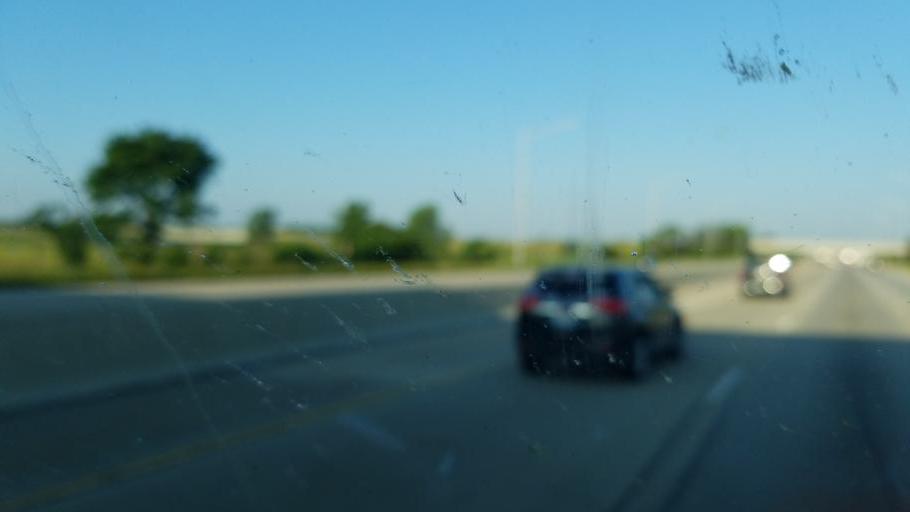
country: US
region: Illinois
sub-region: Will County
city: New Lenox
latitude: 41.5393
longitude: -87.9569
